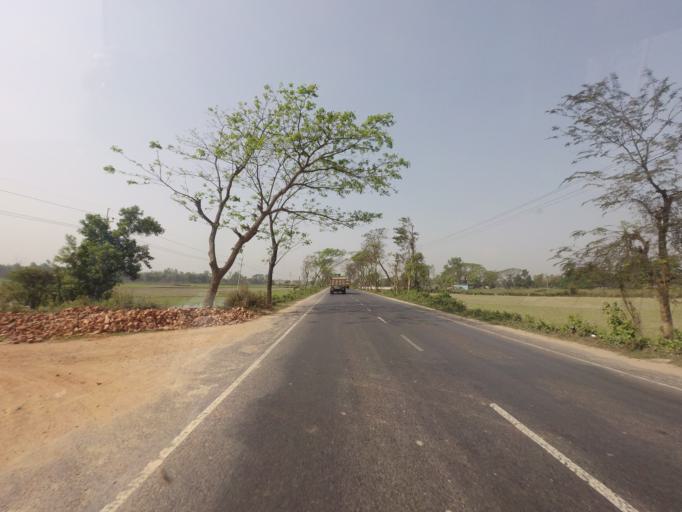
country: BD
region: Sylhet
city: Habiganj
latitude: 24.2847
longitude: 91.4958
